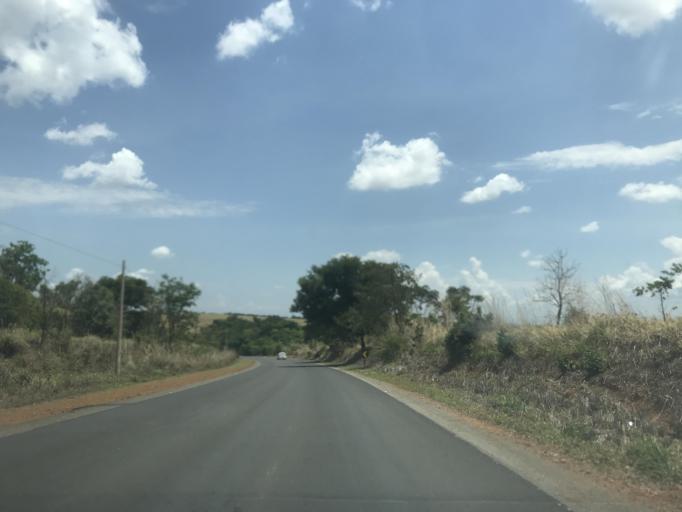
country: BR
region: Goias
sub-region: Bela Vista De Goias
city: Bela Vista de Goias
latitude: -17.0771
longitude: -48.6575
